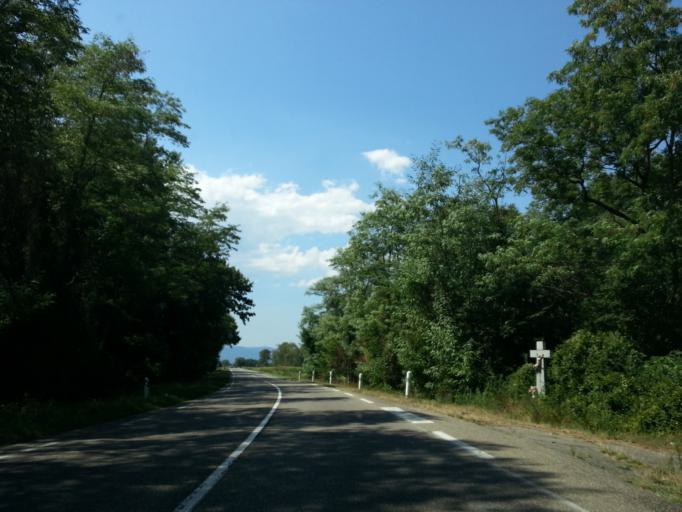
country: FR
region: Alsace
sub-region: Departement du Haut-Rhin
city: Andolsheim
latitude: 48.0544
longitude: 7.4468
